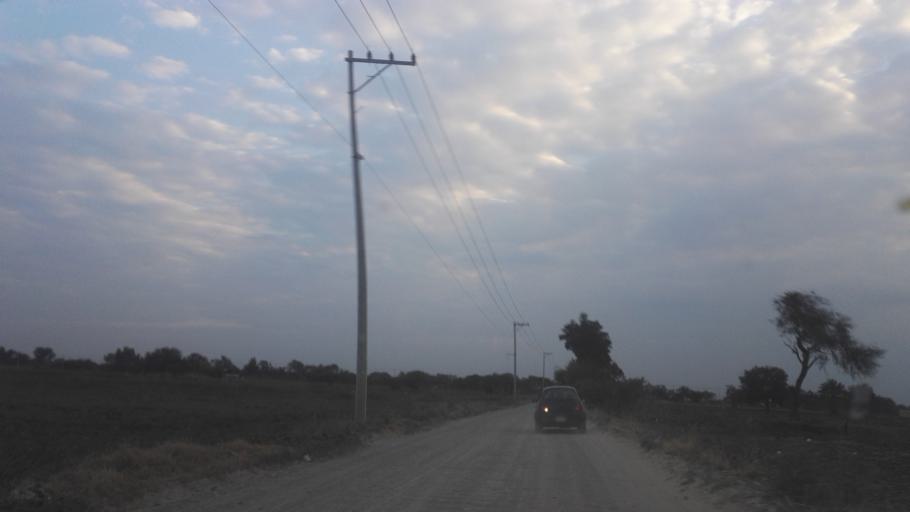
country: MX
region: Guanajuato
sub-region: Leon
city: Ladrilleras del Refugio
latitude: 21.0807
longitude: -101.5569
